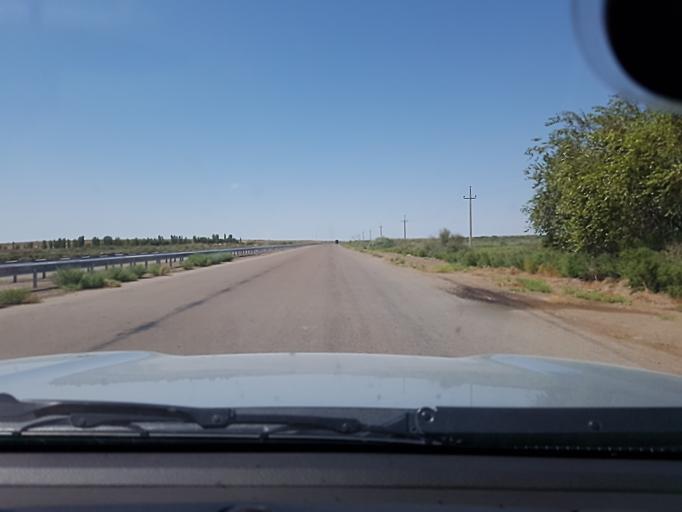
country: TM
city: Akdepe
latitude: 41.7503
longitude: 59.3176
